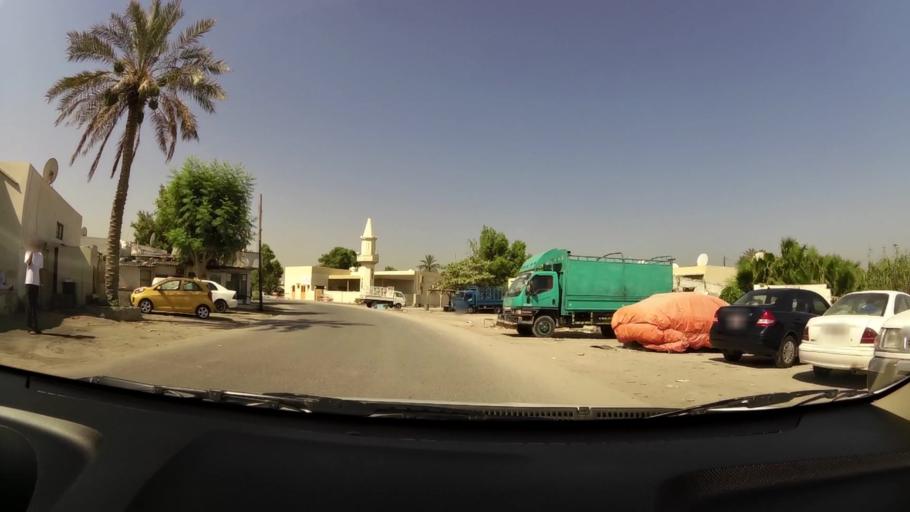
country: AE
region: Umm al Qaywayn
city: Umm al Qaywayn
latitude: 25.5834
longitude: 55.5748
